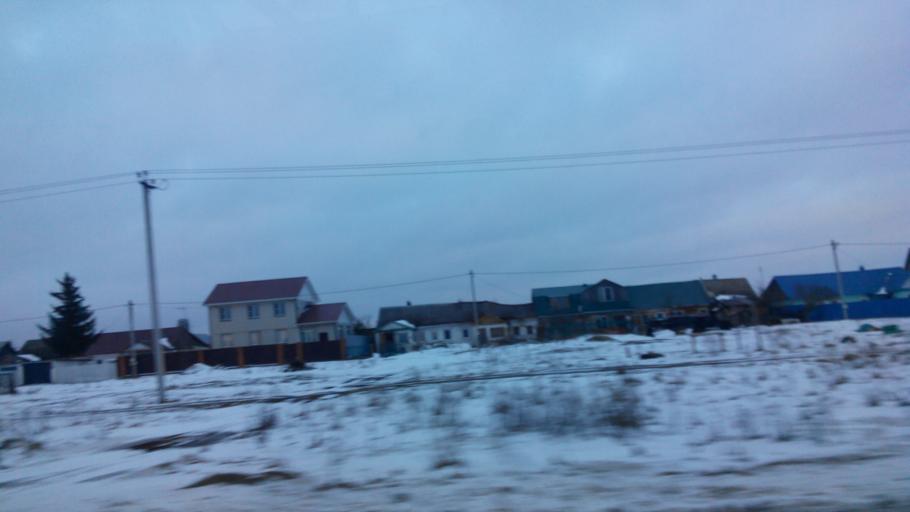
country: RU
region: Tula
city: Mayskiy
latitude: 53.9759
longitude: 38.2394
